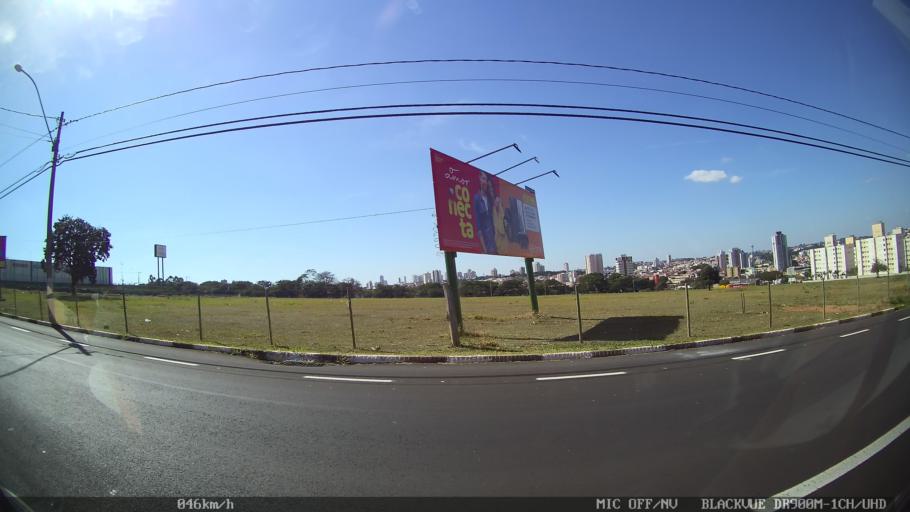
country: BR
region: Sao Paulo
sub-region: Franca
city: Franca
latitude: -20.5508
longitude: -47.4155
